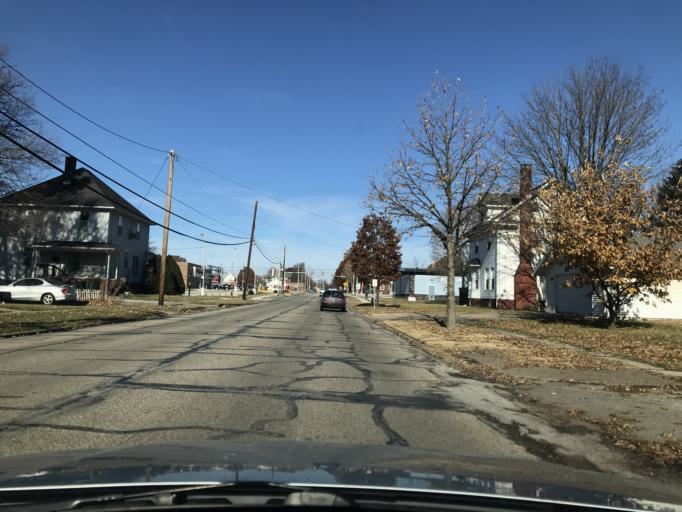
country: US
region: Illinois
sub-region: McDonough County
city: Macomb
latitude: 40.4569
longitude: -90.6672
